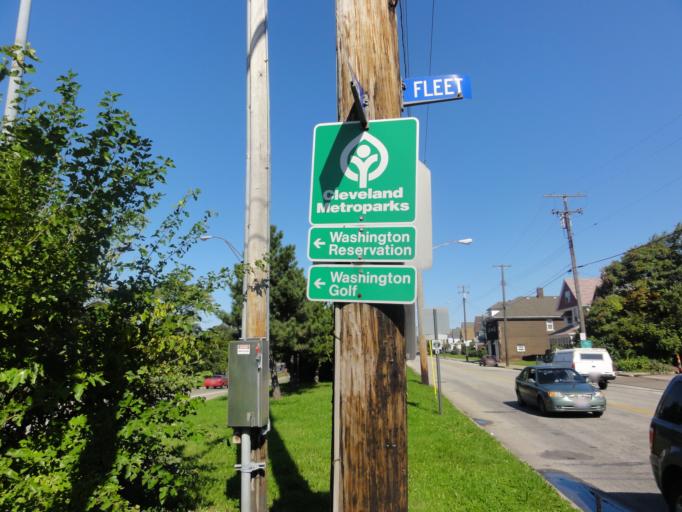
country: US
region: Ohio
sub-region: Cuyahoga County
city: Newburgh Heights
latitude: 41.4556
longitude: -81.6578
